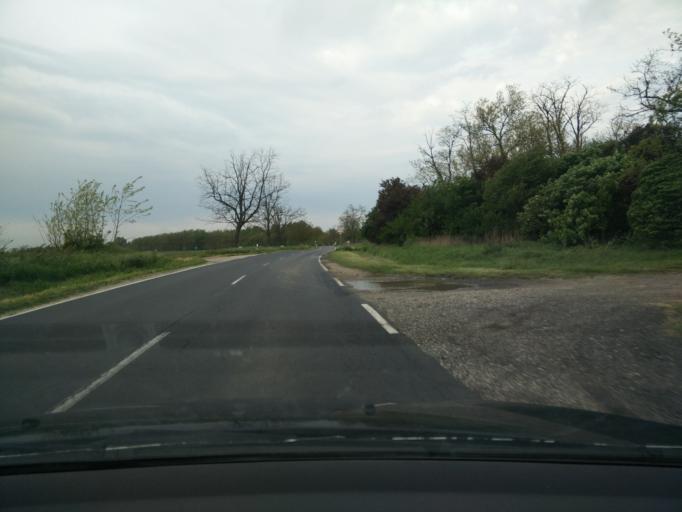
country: HU
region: Gyor-Moson-Sopron
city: Gyorszemere
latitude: 47.5974
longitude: 17.5892
